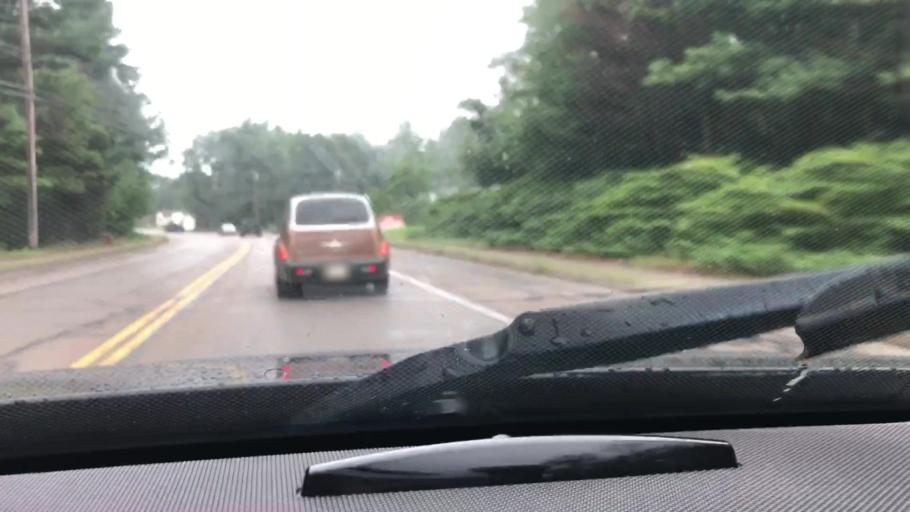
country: US
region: Massachusetts
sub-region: Norfolk County
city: Bellingham
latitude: 42.1089
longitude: -71.4736
